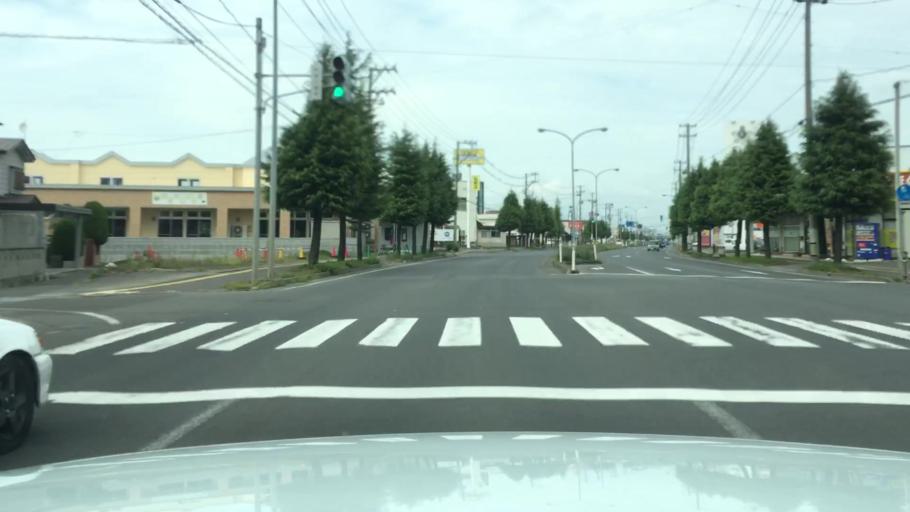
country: JP
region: Aomori
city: Hirosaki
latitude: 40.6120
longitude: 140.4823
